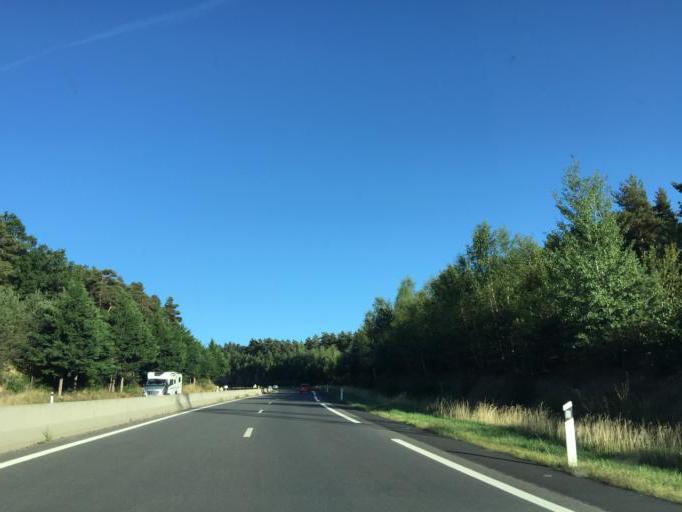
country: FR
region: Auvergne
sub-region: Departement de la Haute-Loire
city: Blavozy
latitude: 45.0645
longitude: 3.9835
